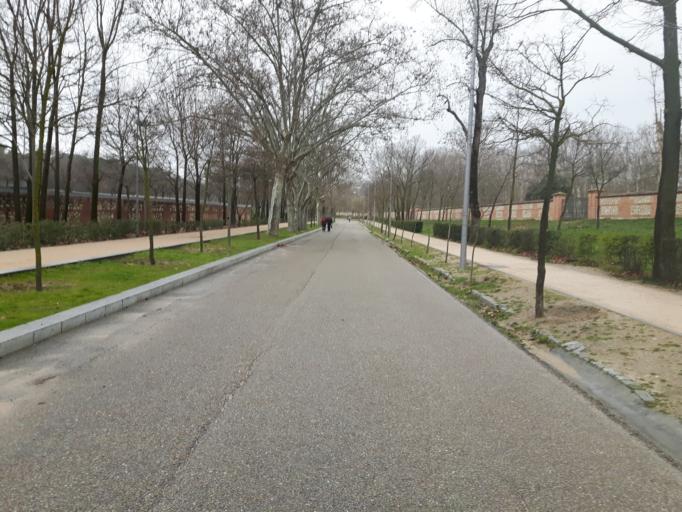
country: ES
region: Madrid
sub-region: Provincia de Madrid
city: Moncloa-Aravaca
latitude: 40.4186
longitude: -3.7251
